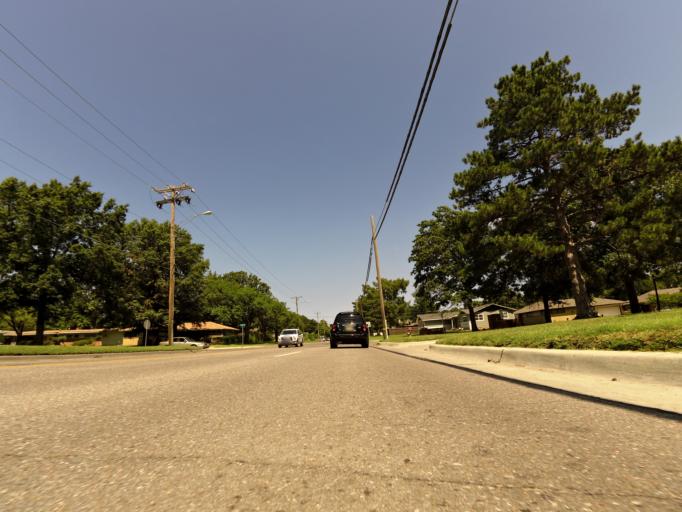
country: US
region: Kansas
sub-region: Sedgwick County
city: Bellaire
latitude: 37.7007
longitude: -97.2622
